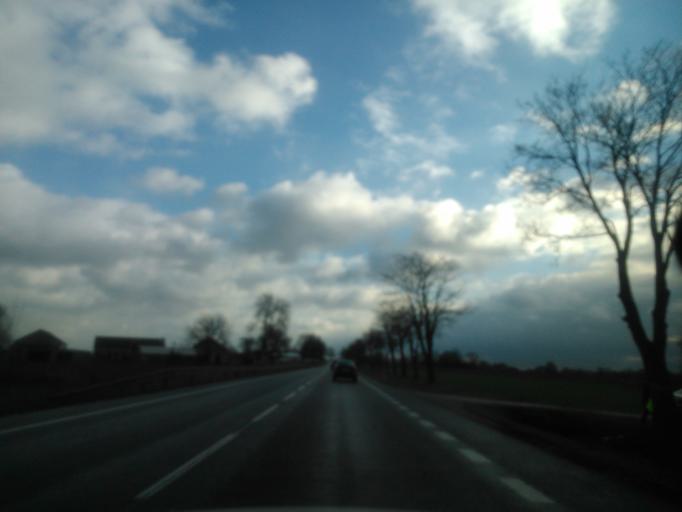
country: PL
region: Masovian Voivodeship
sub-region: Powiat sierpecki
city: Rosciszewo
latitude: 52.8218
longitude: 19.7761
